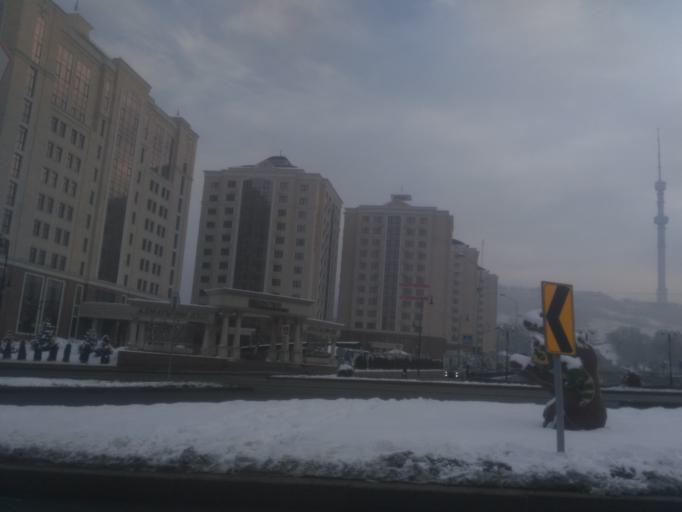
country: KZ
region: Almaty Qalasy
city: Almaty
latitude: 43.2289
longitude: 76.9603
